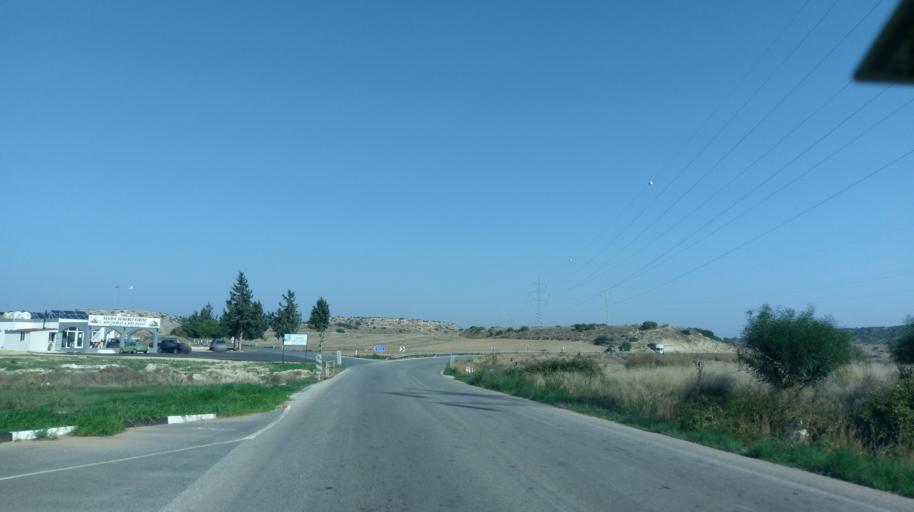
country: CY
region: Ammochostos
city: Leonarisso
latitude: 35.3818
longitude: 34.0410
